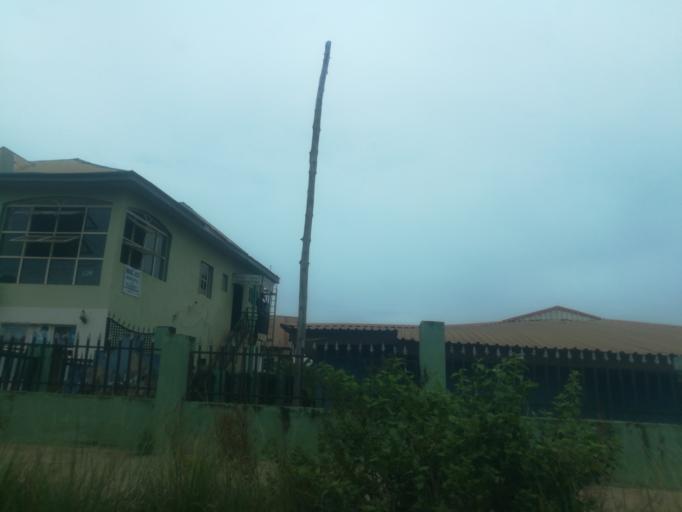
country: NG
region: Oyo
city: Ibadan
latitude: 7.3291
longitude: 3.8924
